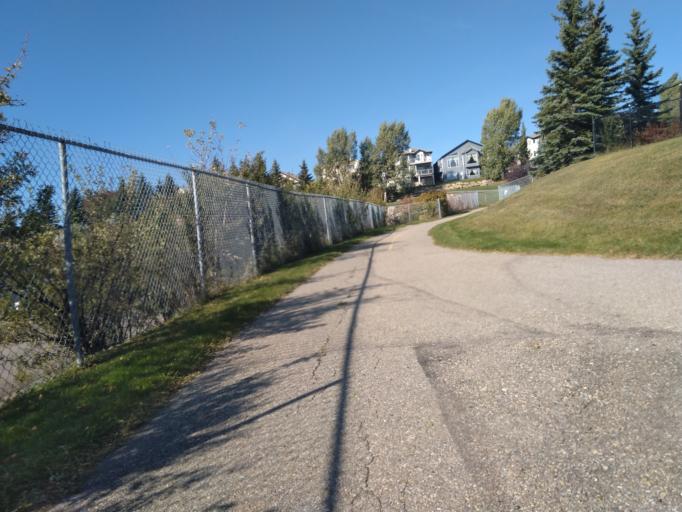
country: CA
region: Alberta
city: Calgary
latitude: 51.1469
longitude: -114.0845
